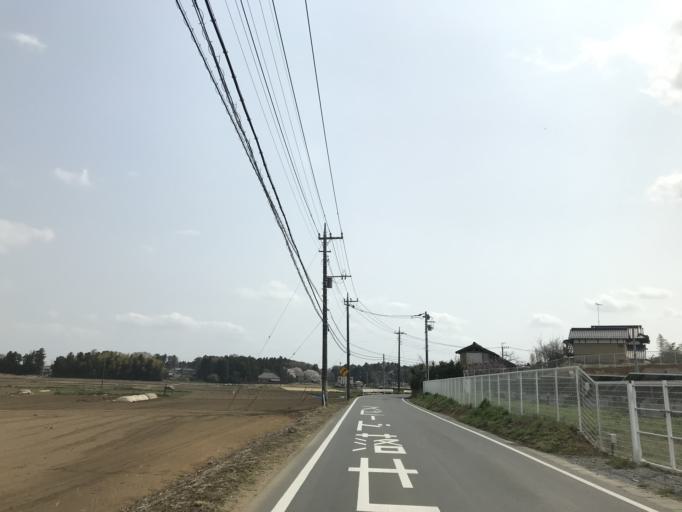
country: JP
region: Ibaraki
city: Ushiku
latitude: 36.0083
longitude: 140.0660
